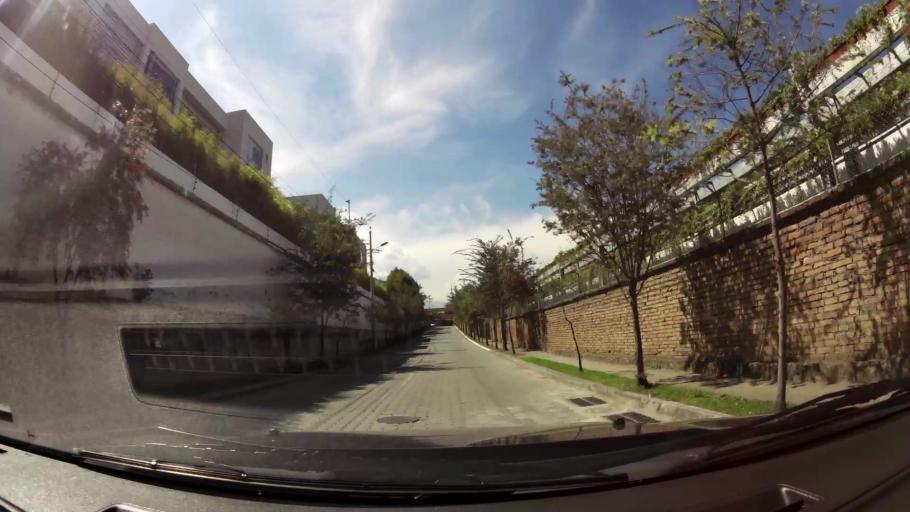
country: EC
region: Pichincha
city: Quito
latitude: -0.2043
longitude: -78.4239
